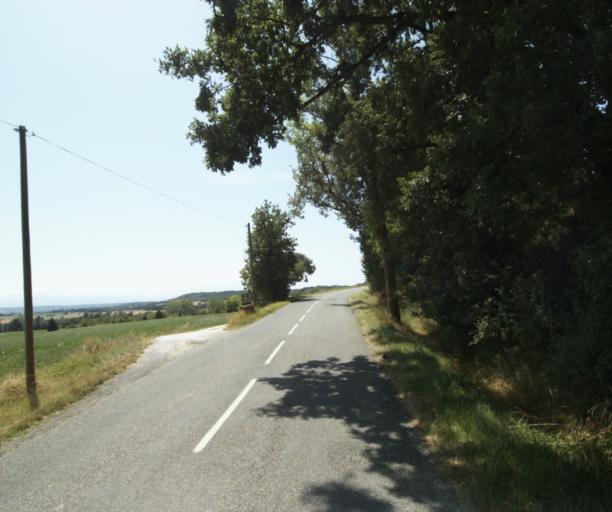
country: FR
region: Midi-Pyrenees
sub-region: Departement de la Haute-Garonne
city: Saint-Felix-Lauragais
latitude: 43.4299
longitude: 1.8886
